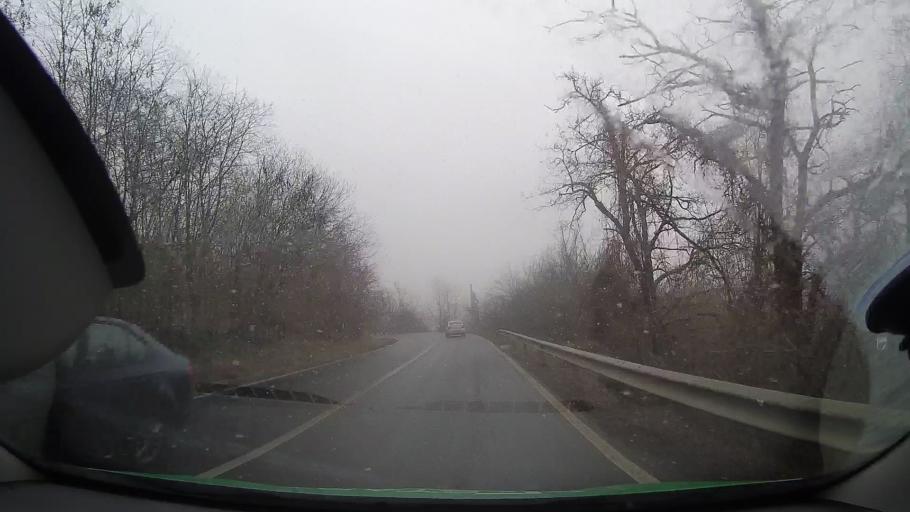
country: RO
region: Sibiu
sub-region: Municipiul Medias
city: Medias
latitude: 46.1816
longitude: 24.3335
